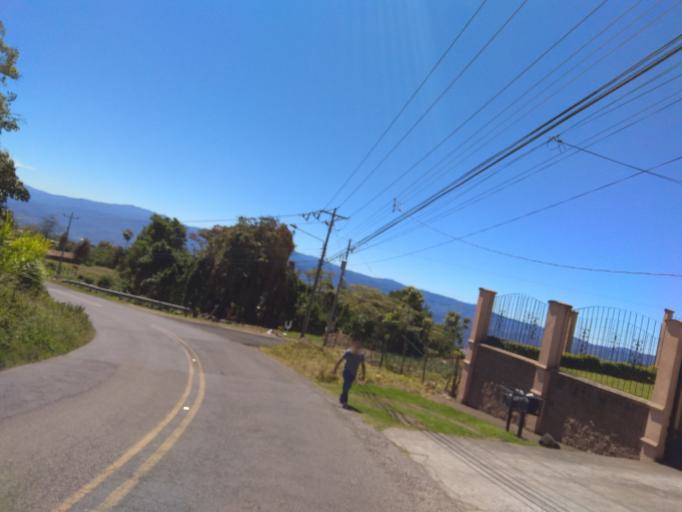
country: CR
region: Cartago
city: Cot
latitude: 9.9215
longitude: -83.9161
